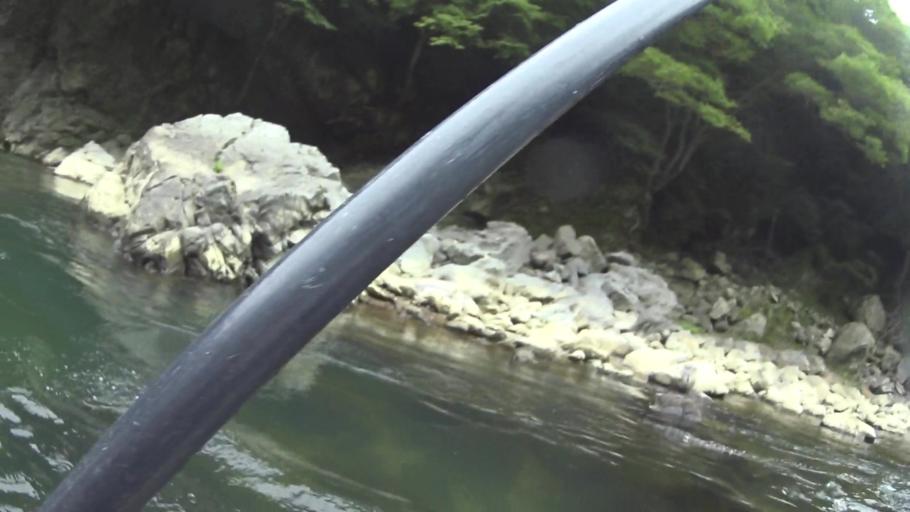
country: JP
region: Kyoto
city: Kameoka
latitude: 35.0201
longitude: 135.6263
